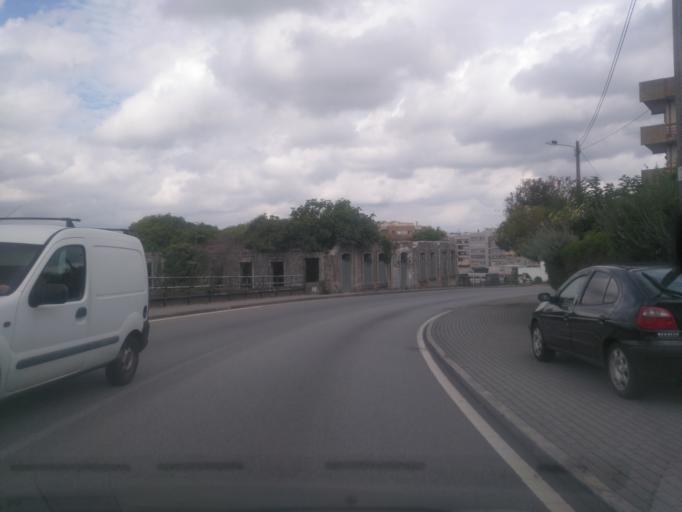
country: PT
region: Braga
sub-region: Braga
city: Braga
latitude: 41.5505
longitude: -8.4379
